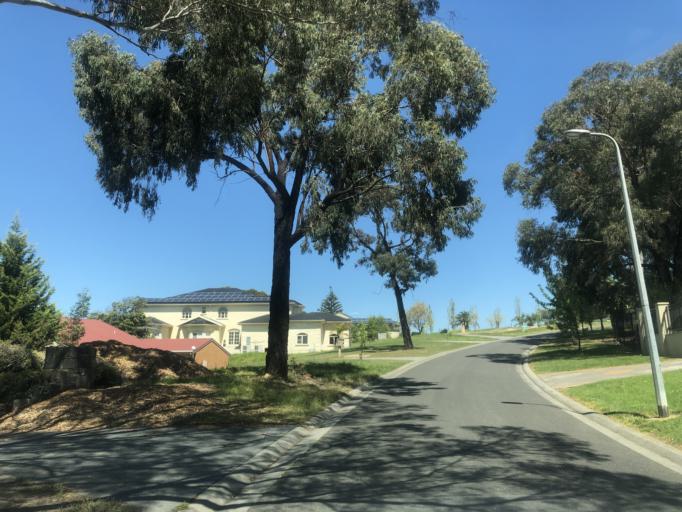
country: AU
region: Victoria
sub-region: Casey
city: Narre Warren North
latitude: -37.9827
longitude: 145.2881
